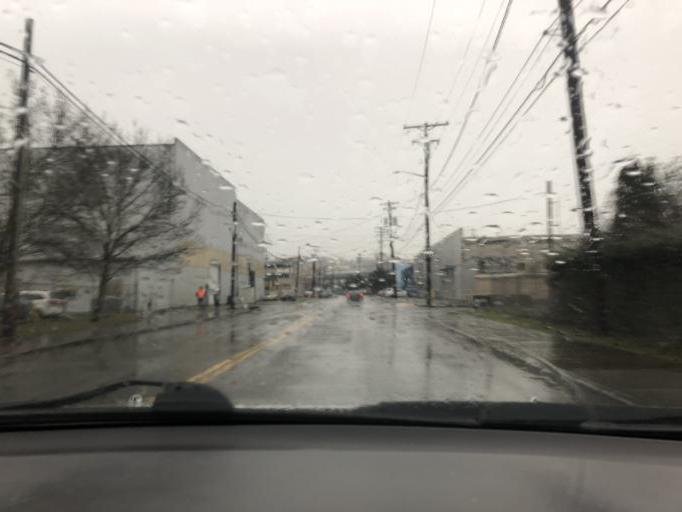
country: US
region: Washington
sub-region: Pierce County
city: Tacoma
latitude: 47.2537
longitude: -122.4254
